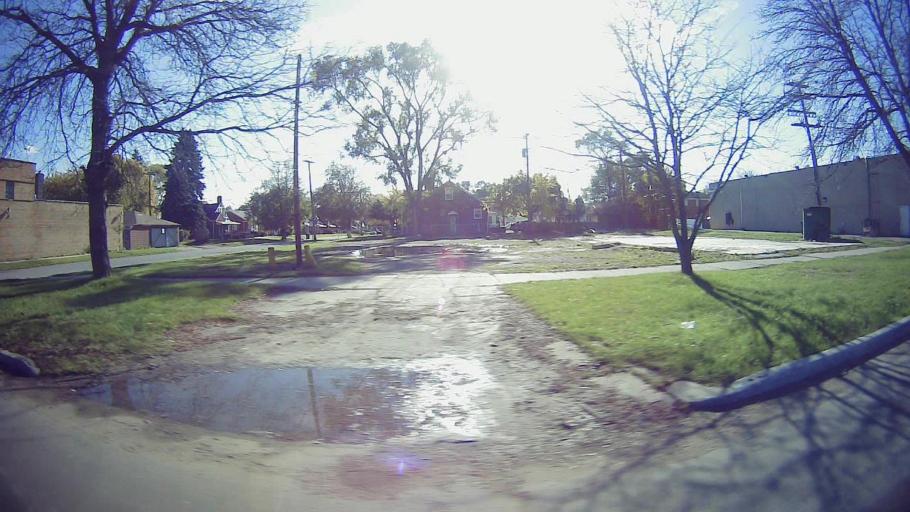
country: US
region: Michigan
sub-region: Wayne County
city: Dearborn
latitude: 42.3585
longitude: -83.1771
